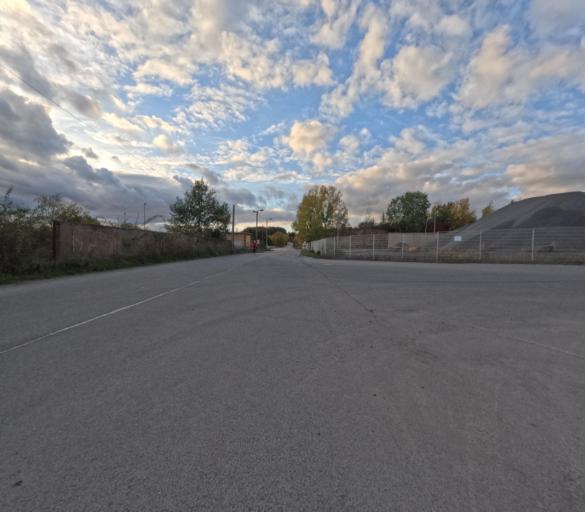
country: DE
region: Saxony
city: Otterwisch
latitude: 51.2501
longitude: 12.6505
